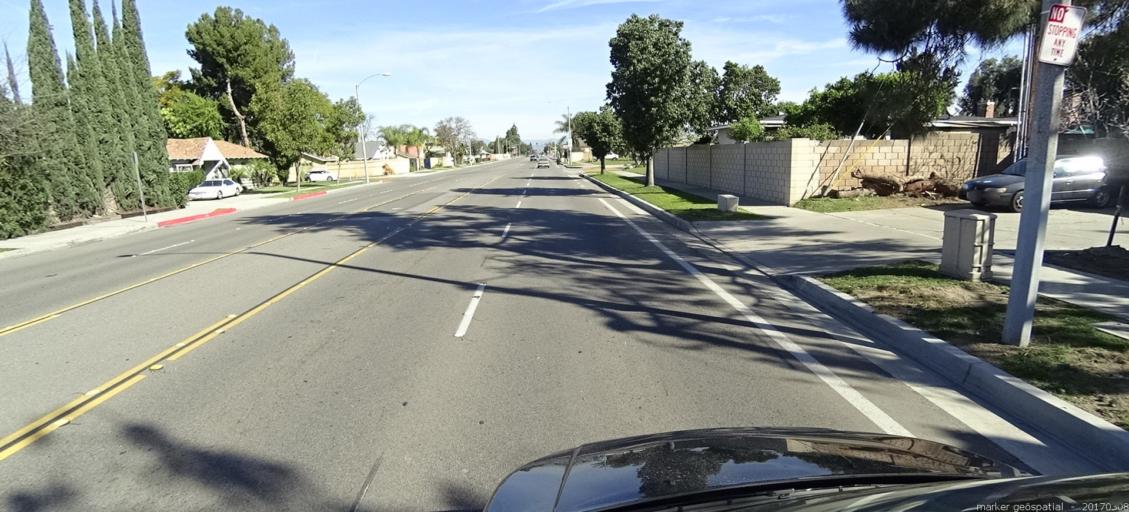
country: US
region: California
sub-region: Orange County
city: Stanton
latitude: 33.8189
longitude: -118.0020
